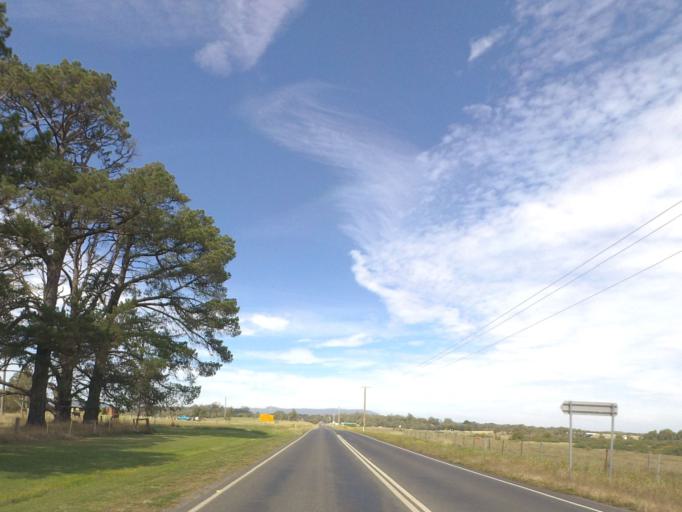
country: AU
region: Victoria
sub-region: Mount Alexander
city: Castlemaine
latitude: -37.2868
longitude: 144.5015
